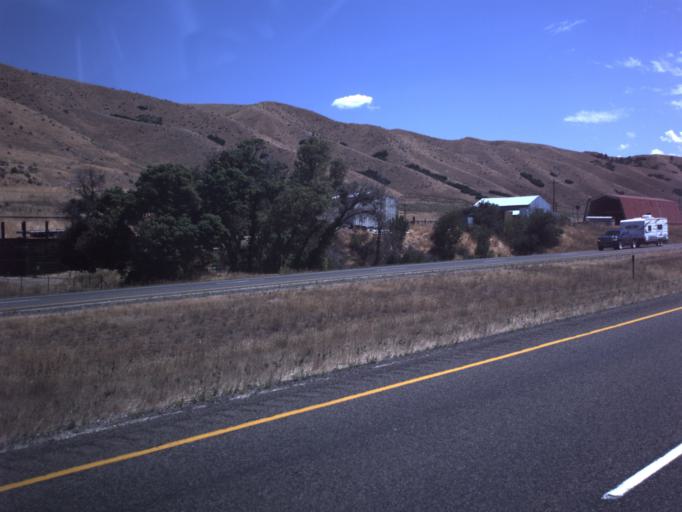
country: US
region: Utah
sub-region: Summit County
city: Coalville
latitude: 40.9936
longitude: -111.4613
